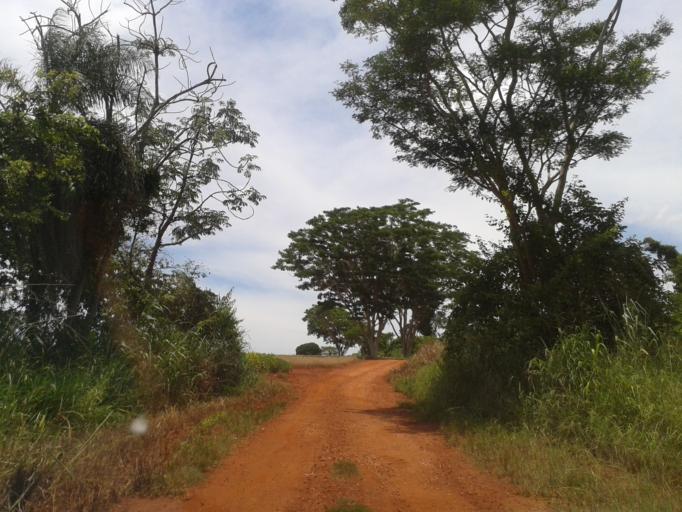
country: BR
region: Minas Gerais
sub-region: Capinopolis
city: Capinopolis
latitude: -18.6603
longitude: -49.7334
